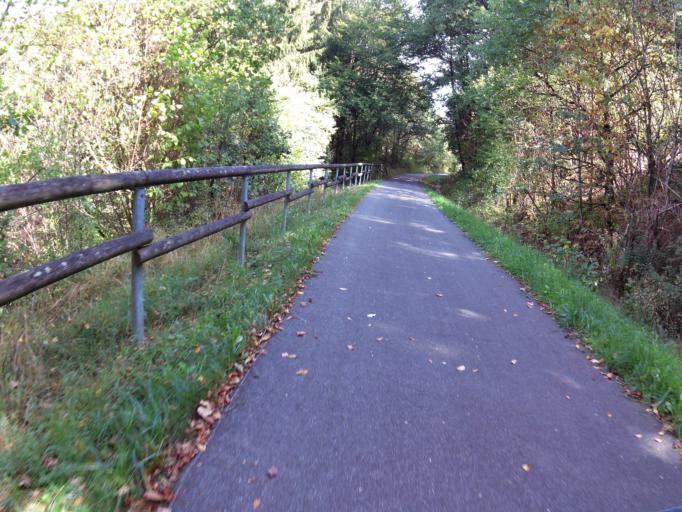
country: DE
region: Rheinland-Pfalz
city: Arzfeld
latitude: 50.0750
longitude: 6.2595
